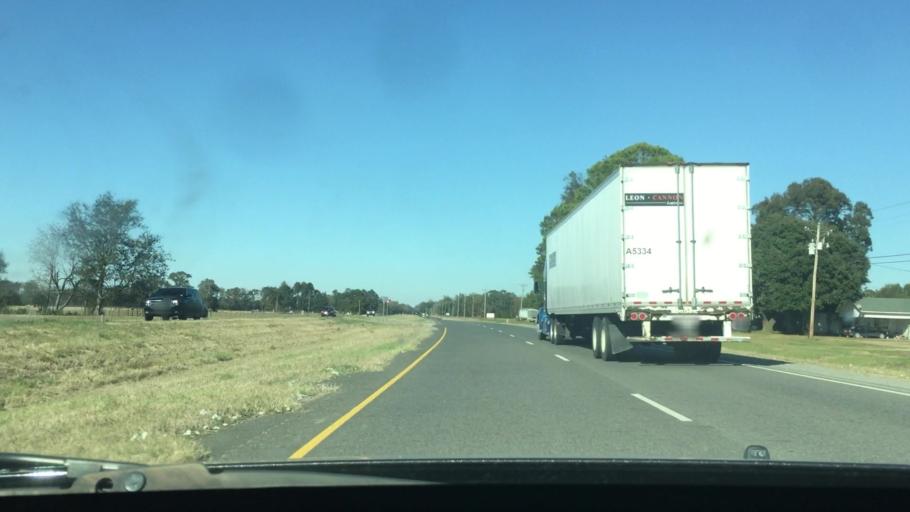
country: US
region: Louisiana
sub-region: Richland Parish
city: Rayville
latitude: 32.3788
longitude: -91.7695
